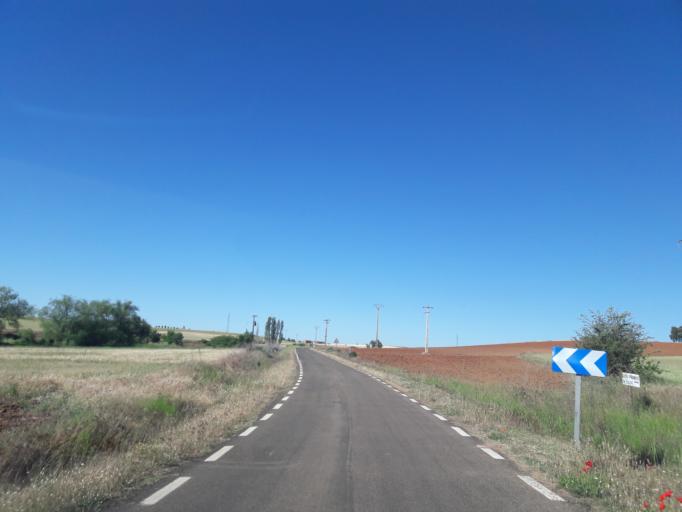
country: ES
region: Castille and Leon
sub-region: Provincia de Salamanca
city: Parada de Arriba
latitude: 40.9982
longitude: -5.7833
